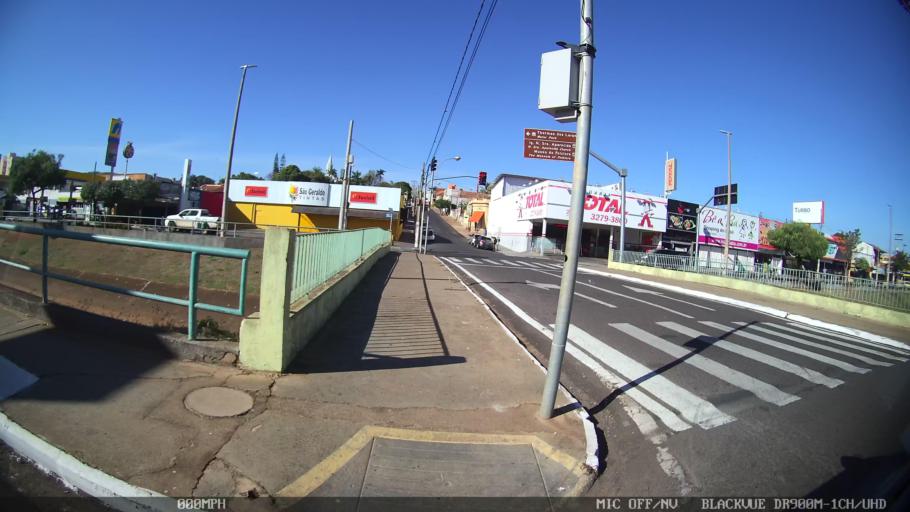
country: BR
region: Sao Paulo
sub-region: Olimpia
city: Olimpia
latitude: -20.7381
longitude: -48.9106
